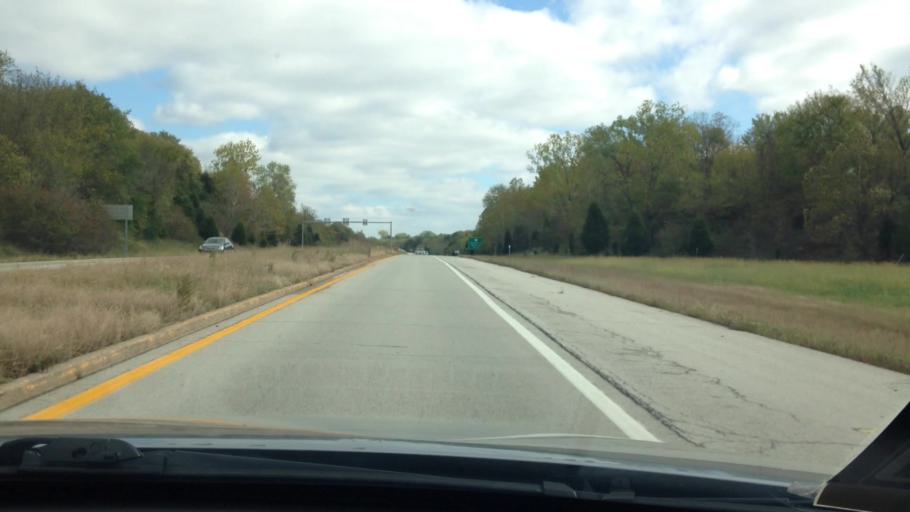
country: US
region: Missouri
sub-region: Platte County
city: Weatherby Lake
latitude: 39.2453
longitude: -94.7539
